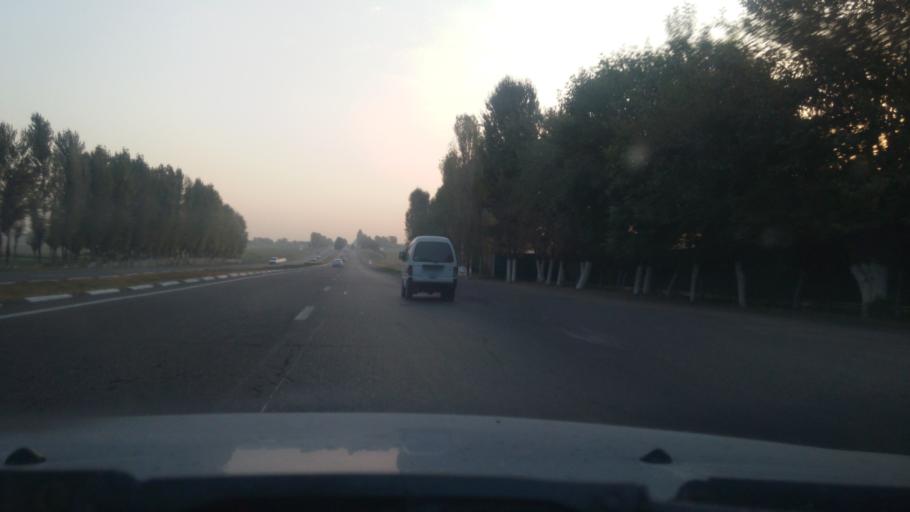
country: UZ
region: Toshkent
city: Amir Timur
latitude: 41.0874
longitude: 68.9480
